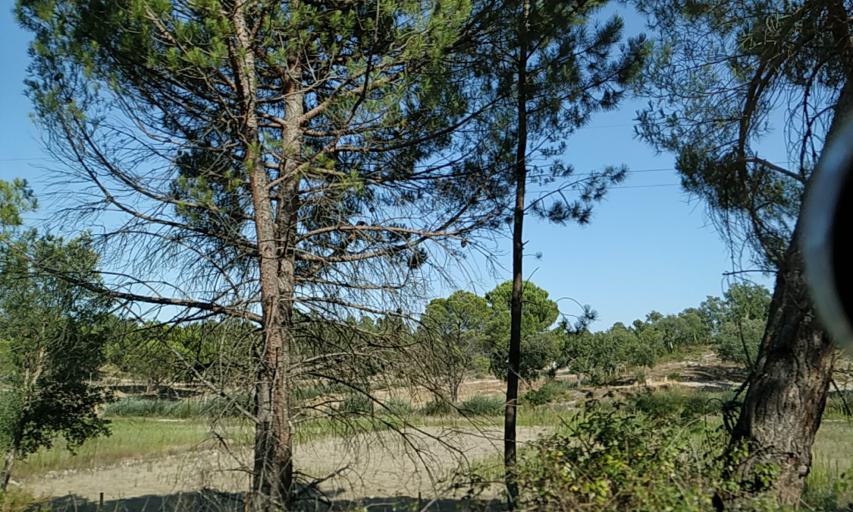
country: PT
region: Evora
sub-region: Vendas Novas
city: Vendas Novas
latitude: 38.7936
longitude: -8.5790
